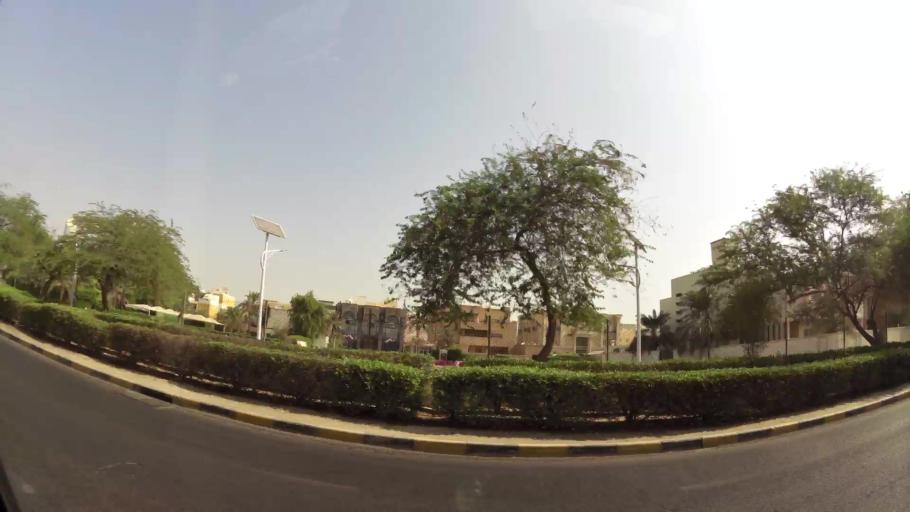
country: KW
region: Al Asimah
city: Kuwait City
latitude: 29.3601
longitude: 47.9880
